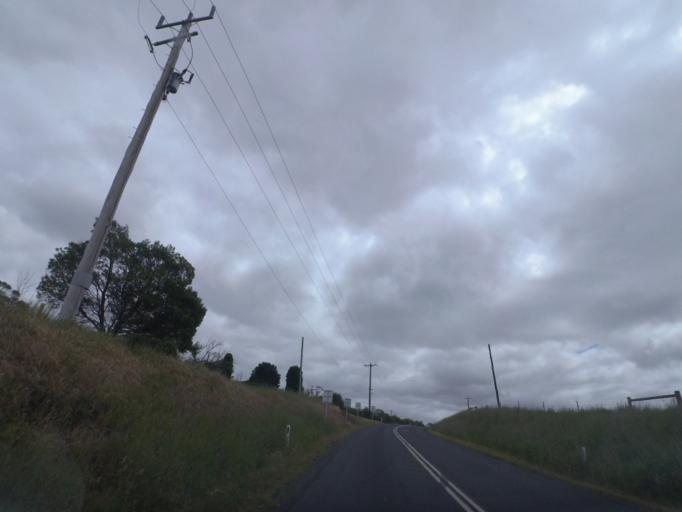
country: AU
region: Victoria
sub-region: Whittlesea
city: Whittlesea
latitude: -37.1883
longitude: 145.0385
